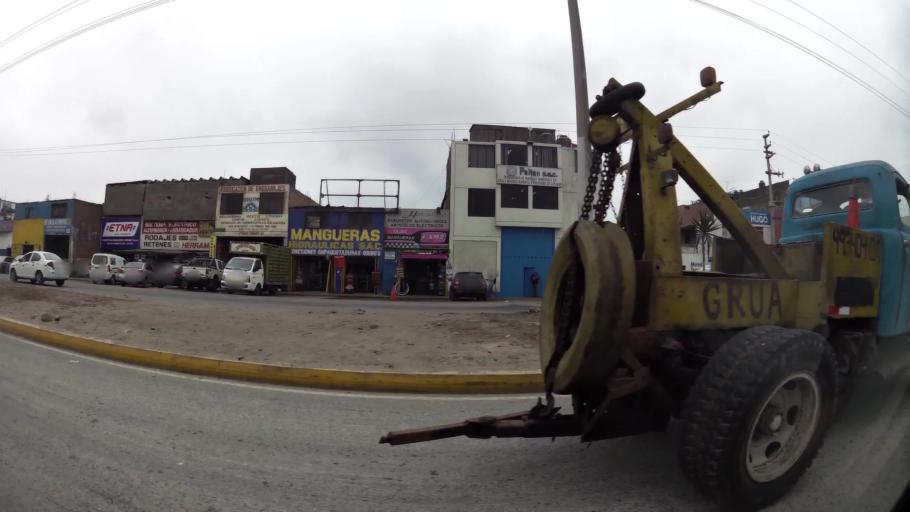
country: PE
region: Callao
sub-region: Callao
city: Callao
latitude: -12.0456
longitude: -77.1264
